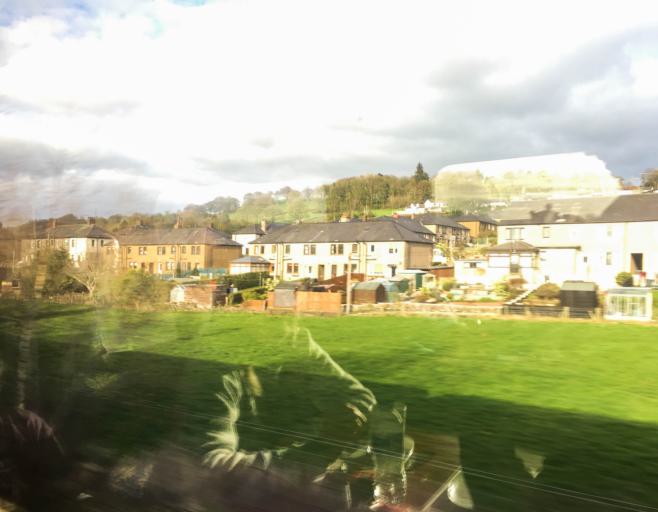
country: GB
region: Scotland
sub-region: Dumfries and Galloway
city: Lockerbie
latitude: 55.1177
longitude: -3.3521
